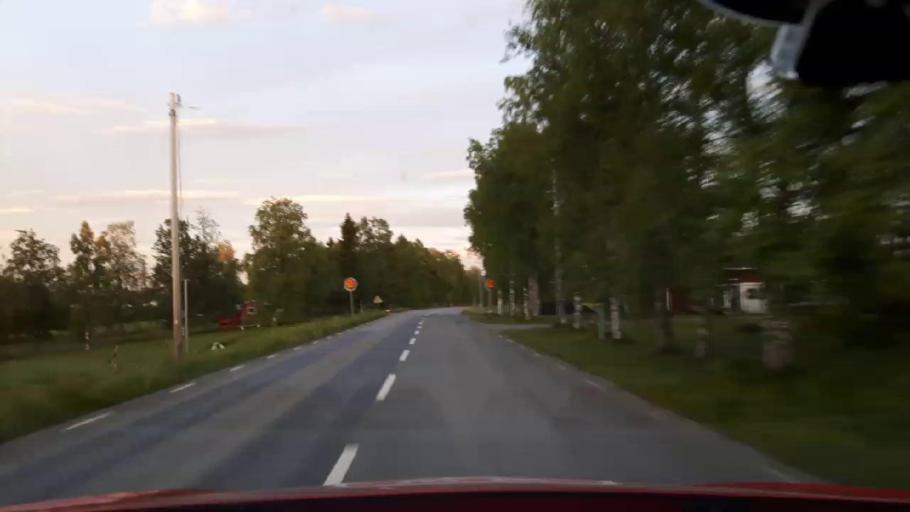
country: SE
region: Jaemtland
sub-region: OEstersunds Kommun
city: Brunflo
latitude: 63.1097
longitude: 14.7333
